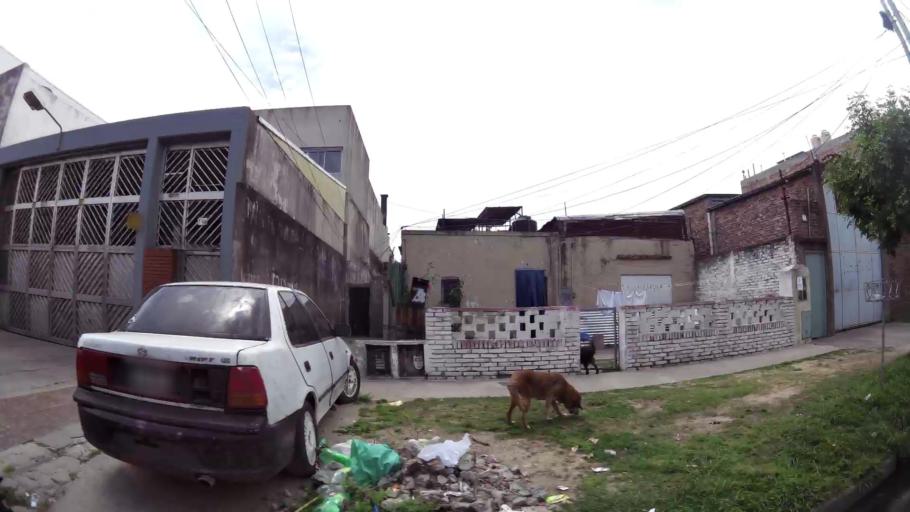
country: AR
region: Buenos Aires
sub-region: Partido de Avellaneda
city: Avellaneda
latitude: -34.6789
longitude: -58.3720
